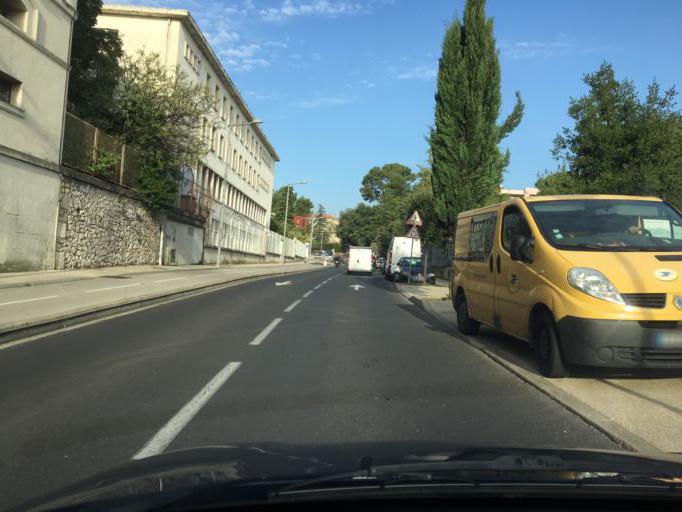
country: FR
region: Languedoc-Roussillon
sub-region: Departement de l'Herault
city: Montpellier
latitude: 43.6221
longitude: 3.8740
